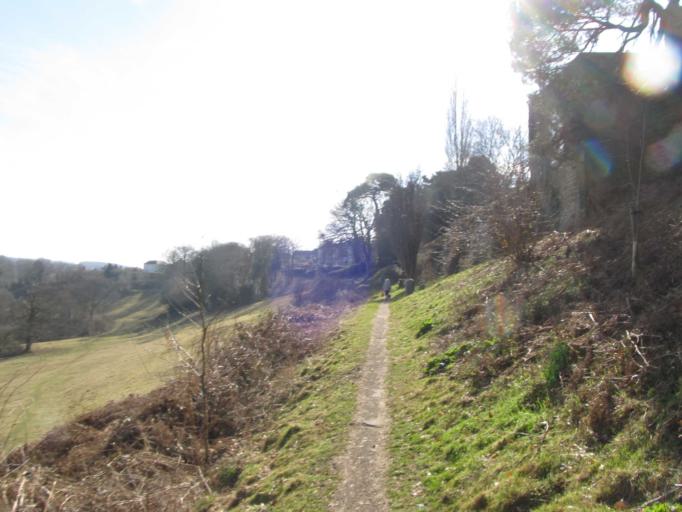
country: GB
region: England
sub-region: West Sussex
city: Petworth
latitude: 50.9872
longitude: -0.6069
